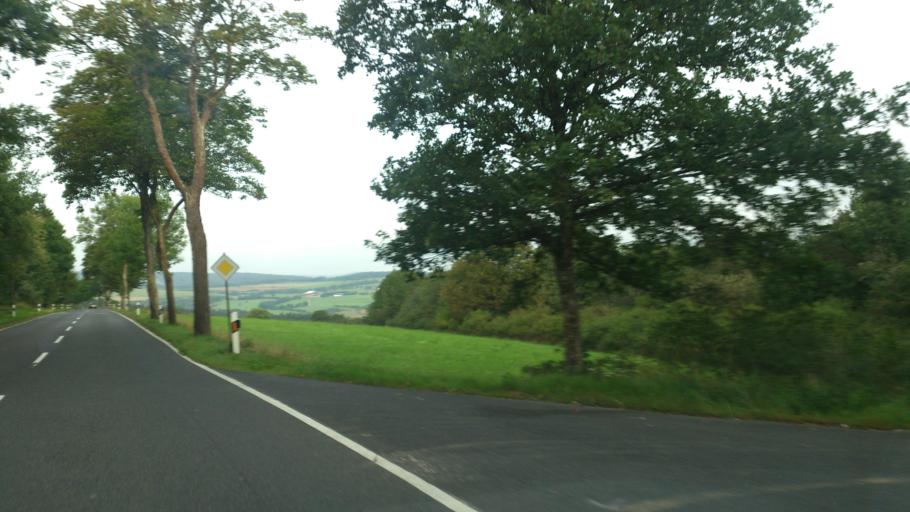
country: DE
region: Rheinland-Pfalz
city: Hoffeld
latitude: 50.3632
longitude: 6.7978
